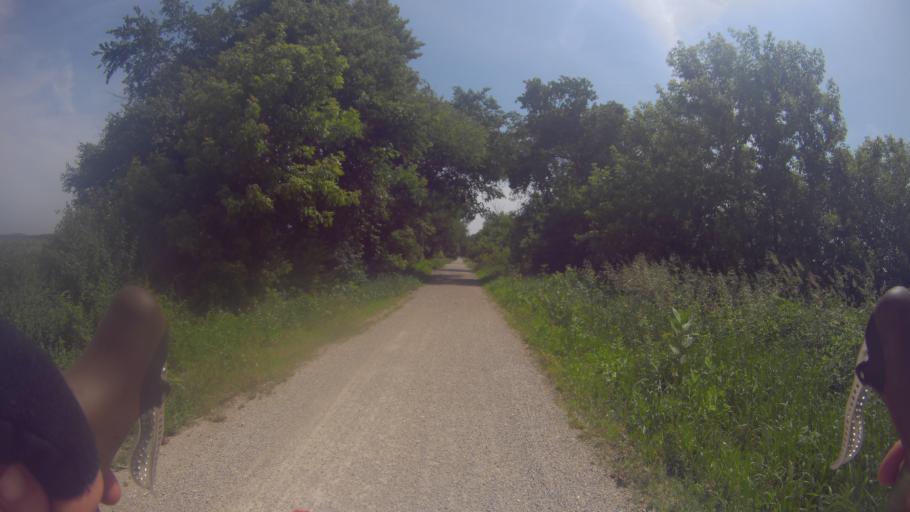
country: US
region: Wisconsin
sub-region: Jefferson County
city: Lake Mills
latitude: 43.0620
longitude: -88.9670
